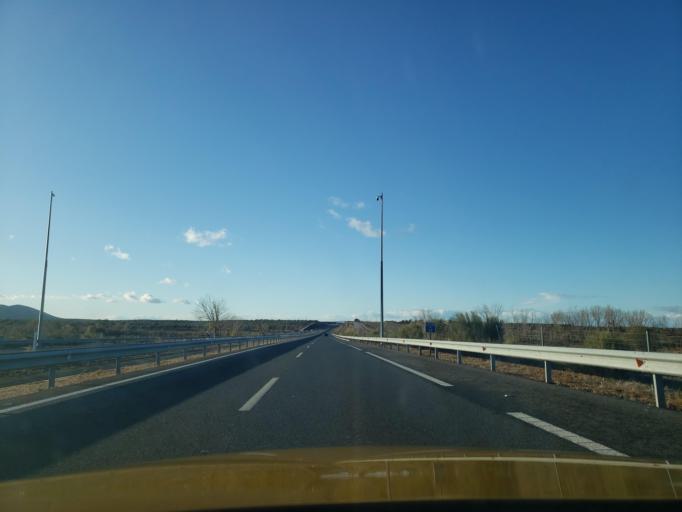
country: ES
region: Castille-La Mancha
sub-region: Province of Toledo
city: Villaminaya
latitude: 39.7664
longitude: -3.8811
